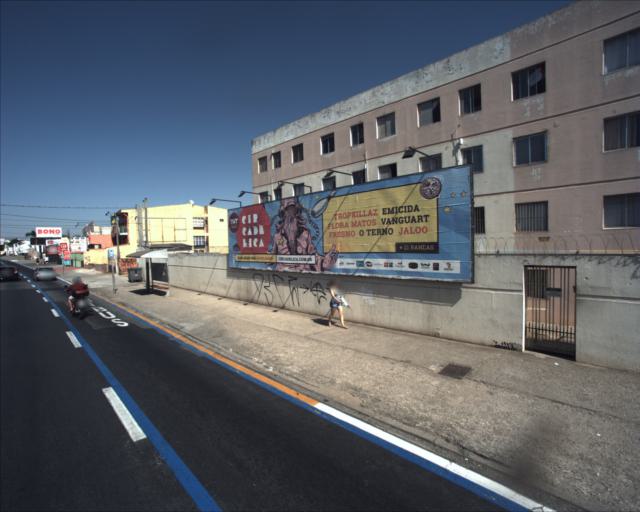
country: BR
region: Sao Paulo
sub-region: Sorocaba
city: Sorocaba
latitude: -23.4654
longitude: -47.4790
